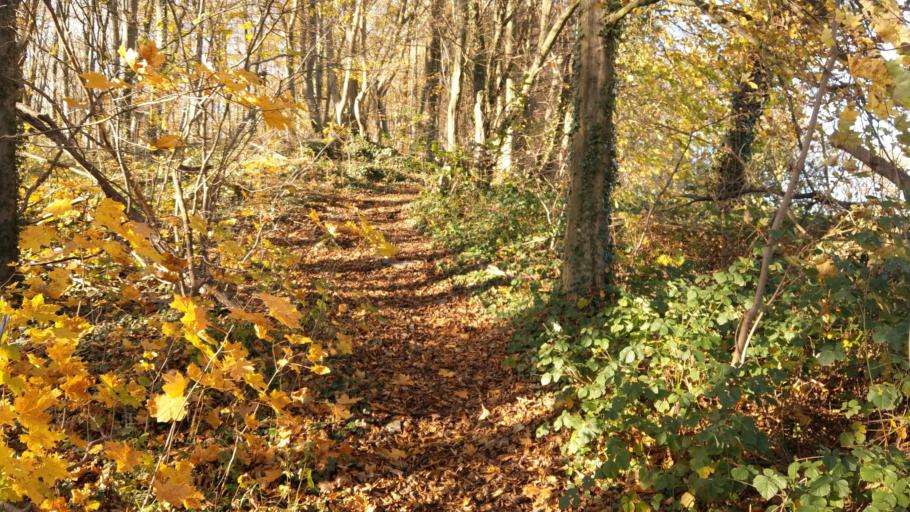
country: BE
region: Wallonia
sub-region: Province de Liege
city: La Calamine
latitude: 50.7078
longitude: 6.0208
